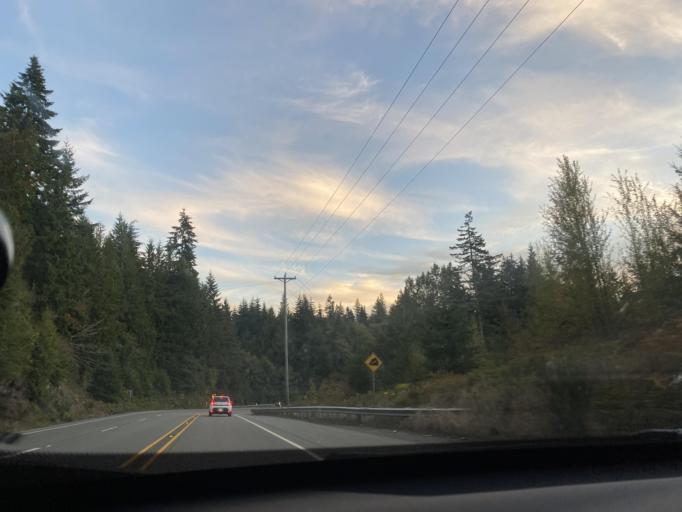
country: US
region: Washington
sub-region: Clallam County
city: Port Angeles
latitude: 48.0832
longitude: -123.5583
